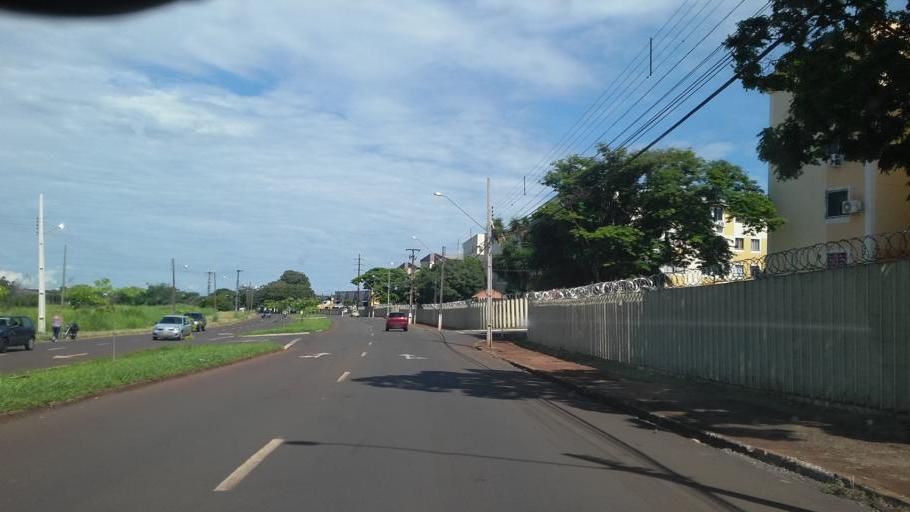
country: BR
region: Parana
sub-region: Londrina
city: Londrina
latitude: -23.2833
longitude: -51.1811
